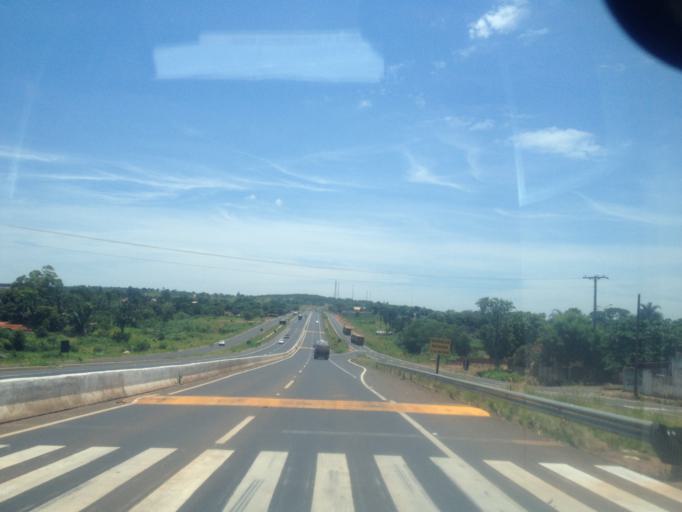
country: BR
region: Minas Gerais
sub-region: Monte Alegre De Minas
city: Monte Alegre de Minas
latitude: -18.8744
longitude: -48.8732
